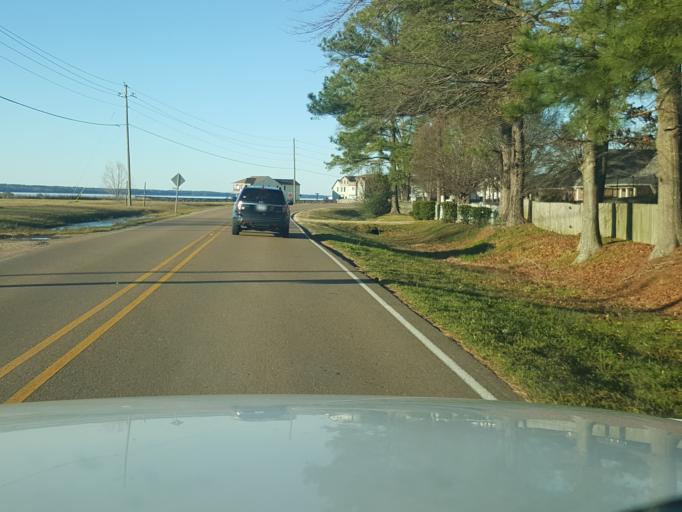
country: US
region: Mississippi
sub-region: Madison County
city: Madison
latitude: 32.4185
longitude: -90.0208
